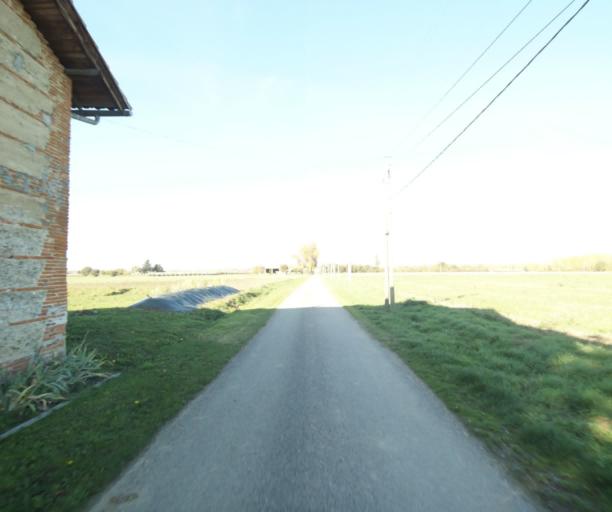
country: FR
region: Midi-Pyrenees
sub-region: Departement du Tarn-et-Garonne
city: Finhan
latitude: 43.9354
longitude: 1.2062
